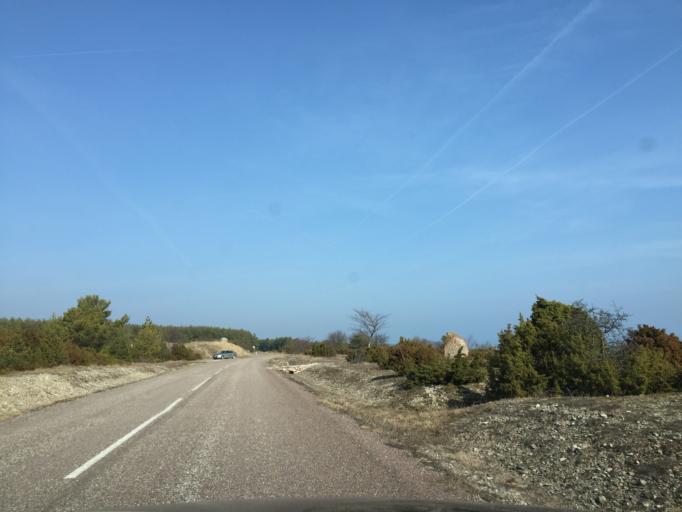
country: LV
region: Dundaga
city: Dundaga
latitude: 57.9167
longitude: 22.0623
